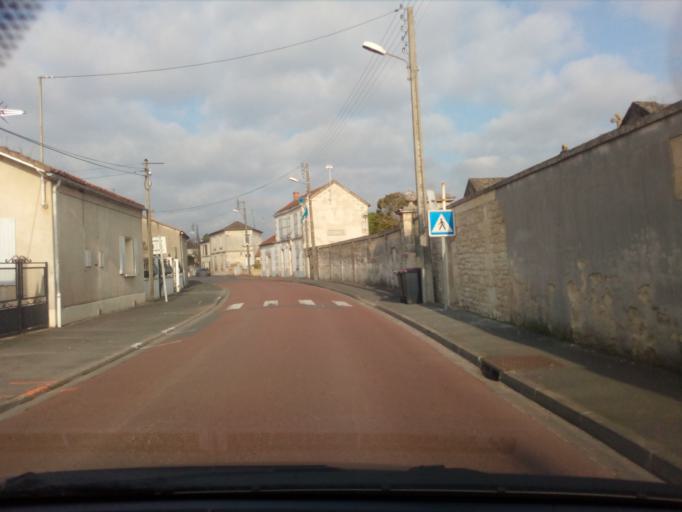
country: FR
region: Poitou-Charentes
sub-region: Departement de la Charente
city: Angouleme
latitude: 45.6646
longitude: 0.1623
